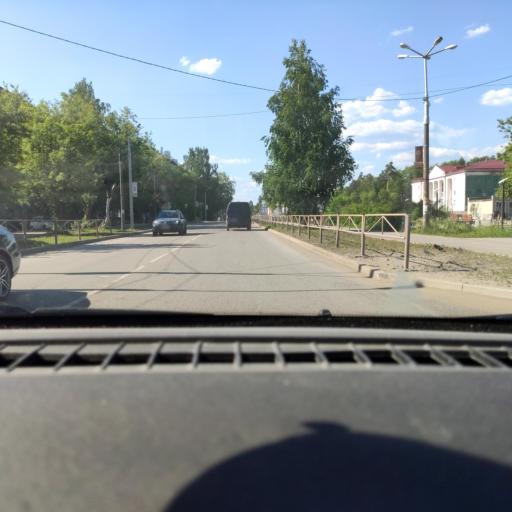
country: RU
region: Perm
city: Krasnokamsk
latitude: 58.0806
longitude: 55.7589
